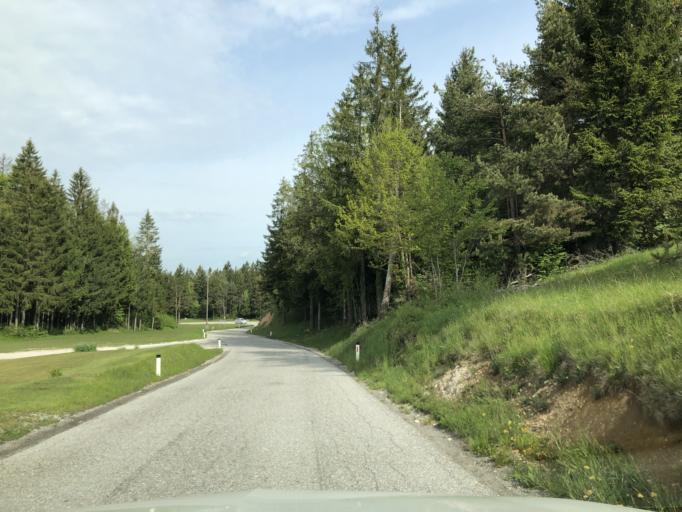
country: SI
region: Bloke
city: Nova Vas
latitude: 45.7976
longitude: 14.5398
